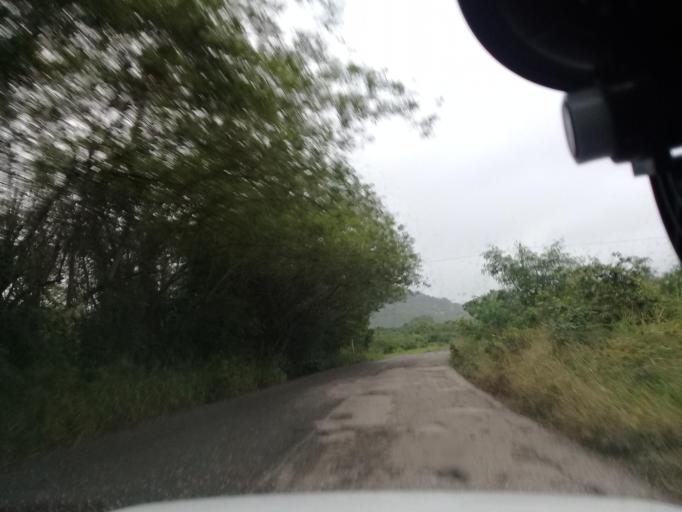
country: MX
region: Veracruz
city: Platon Sanchez
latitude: 21.2241
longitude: -98.3798
